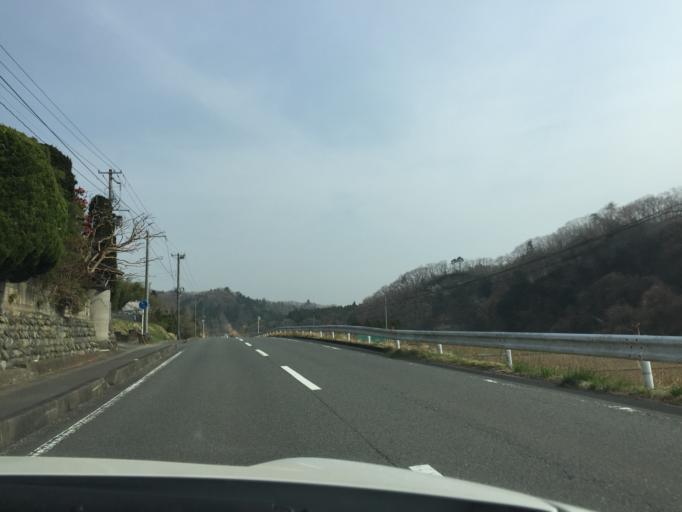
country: JP
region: Fukushima
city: Iwaki
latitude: 36.9948
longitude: 140.7910
